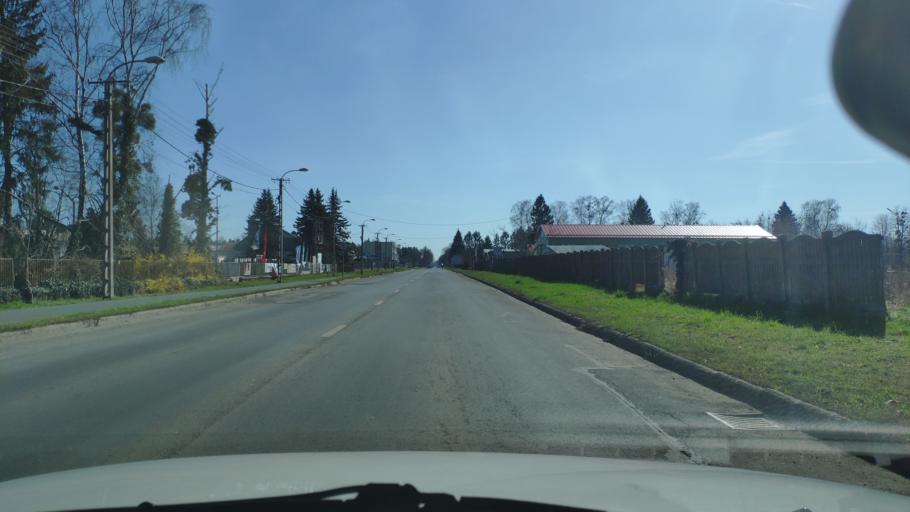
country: HU
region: Zala
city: Nagykanizsa
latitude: 46.4341
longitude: 16.9879
